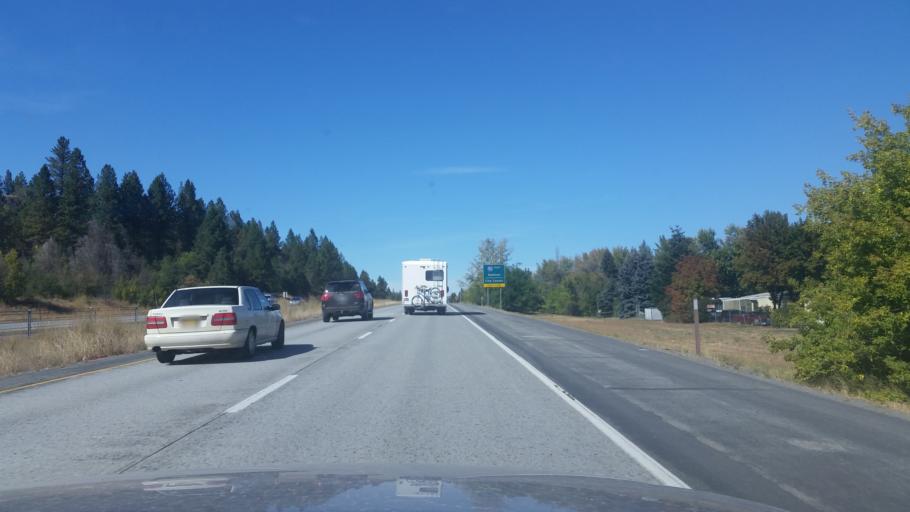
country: US
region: Washington
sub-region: Spokane County
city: Spokane
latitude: 47.6356
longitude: -117.4462
